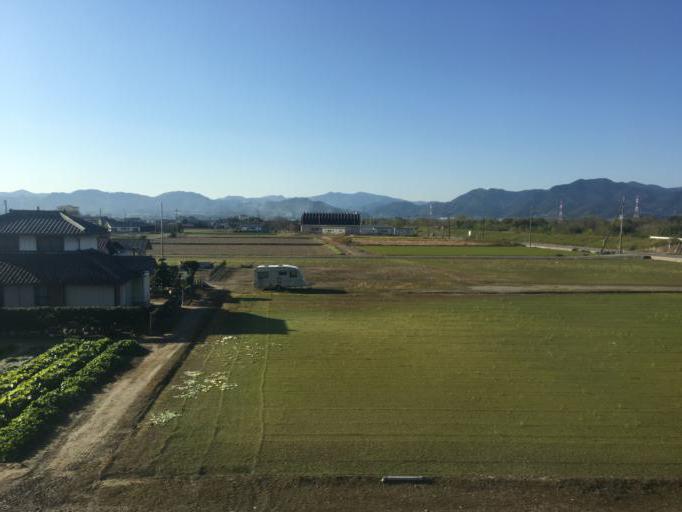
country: JP
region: Gunma
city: Fujioka
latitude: 36.2240
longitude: 139.0913
